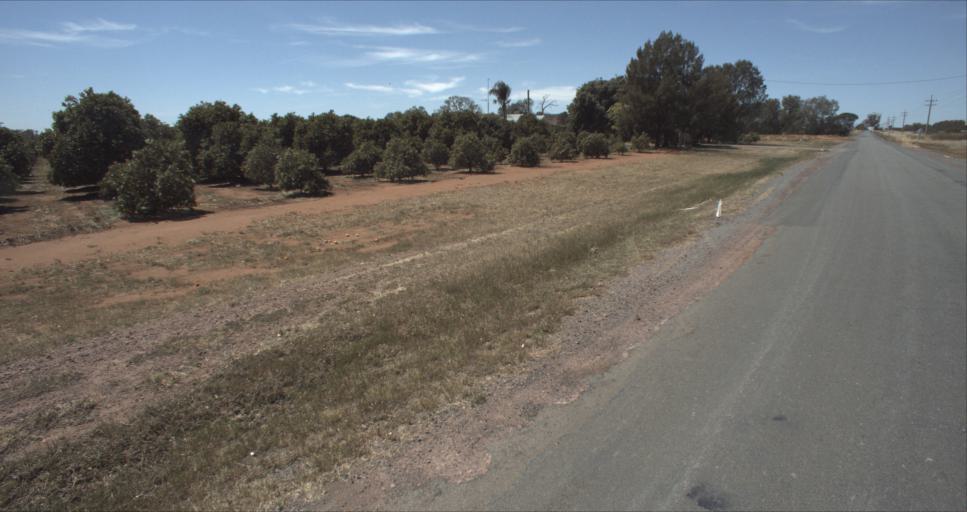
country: AU
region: New South Wales
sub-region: Leeton
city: Leeton
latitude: -34.6115
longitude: 146.4247
